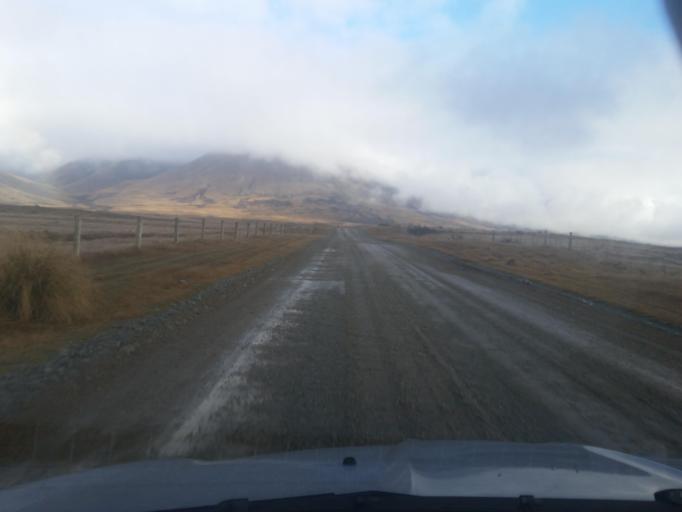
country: NZ
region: Canterbury
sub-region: Ashburton District
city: Methven
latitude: -43.6163
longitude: 171.0876
